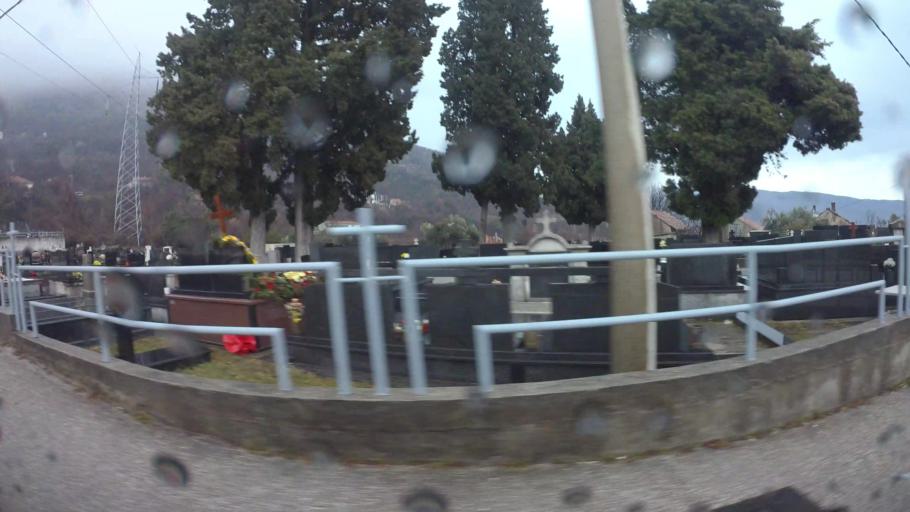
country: BA
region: Federation of Bosnia and Herzegovina
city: Cim
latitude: 43.3555
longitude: 17.7742
